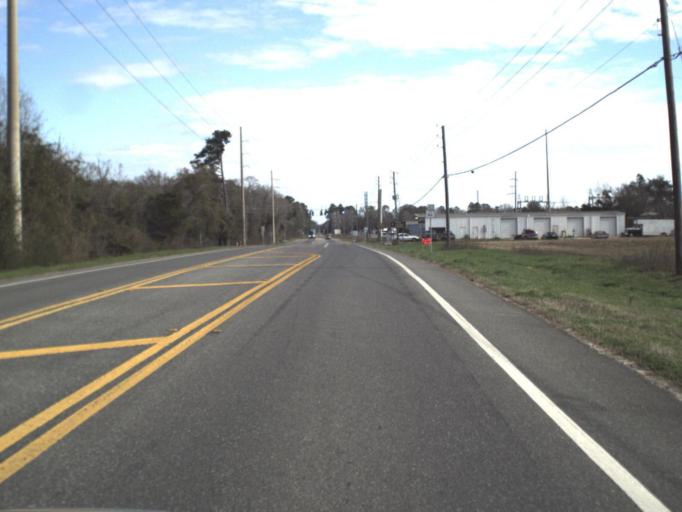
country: US
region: Florida
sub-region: Jackson County
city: Marianna
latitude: 30.8102
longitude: -85.1757
